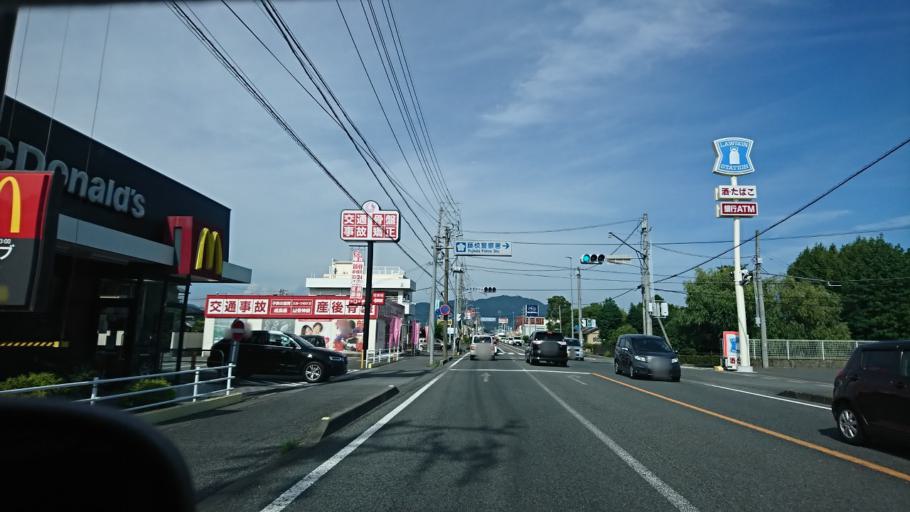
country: JP
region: Shizuoka
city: Fujieda
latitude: 34.8680
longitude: 138.2611
